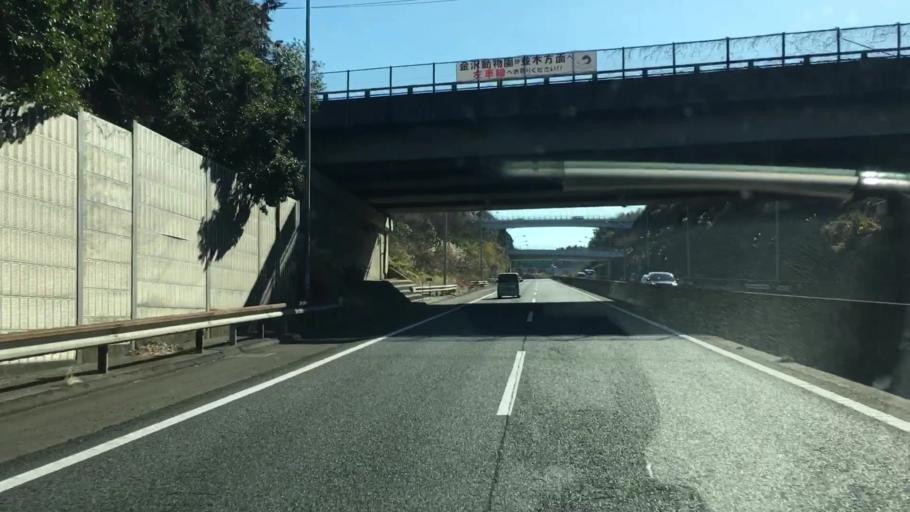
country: JP
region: Kanagawa
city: Kamakura
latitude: 35.3701
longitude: 139.5943
